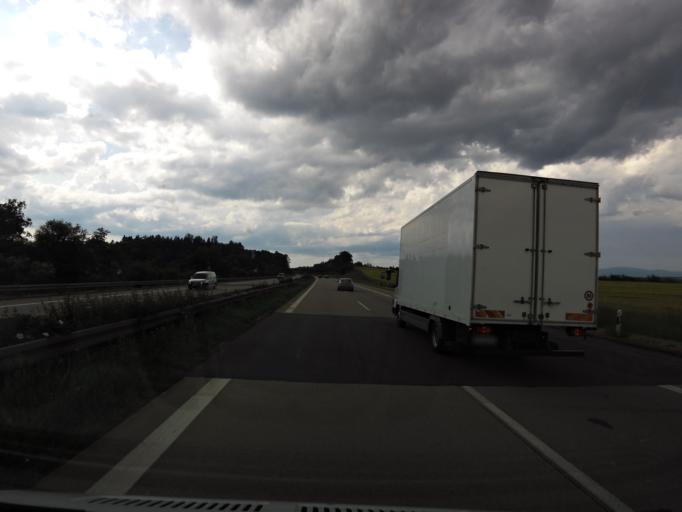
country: DE
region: Bavaria
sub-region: Lower Bavaria
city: Iggensbach
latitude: 48.7349
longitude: 13.1267
